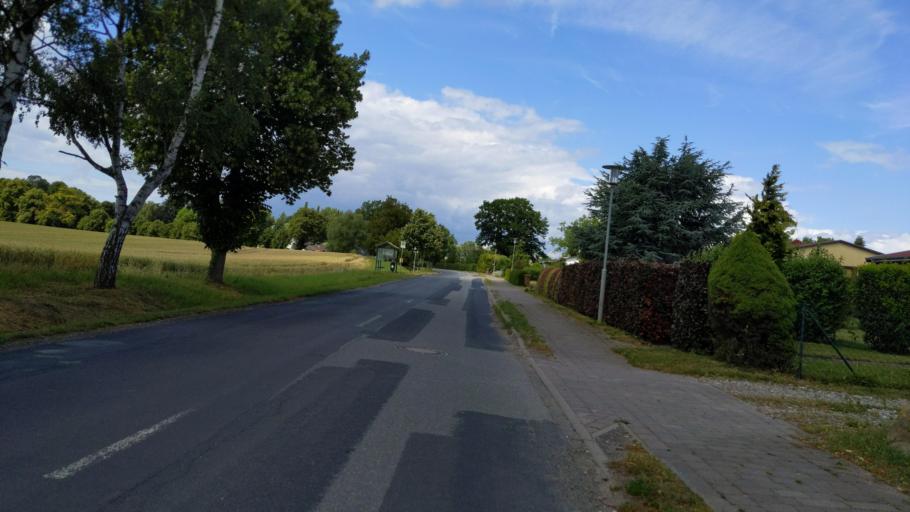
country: DE
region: Mecklenburg-Vorpommern
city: Klutz
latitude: 53.9915
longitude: 11.1248
